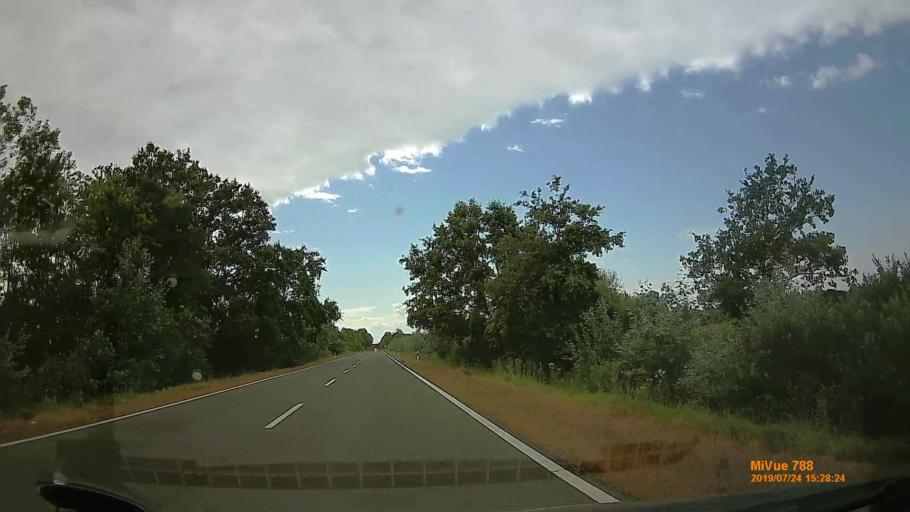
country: HU
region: Szabolcs-Szatmar-Bereg
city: Tarpa
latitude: 48.1610
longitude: 22.4781
